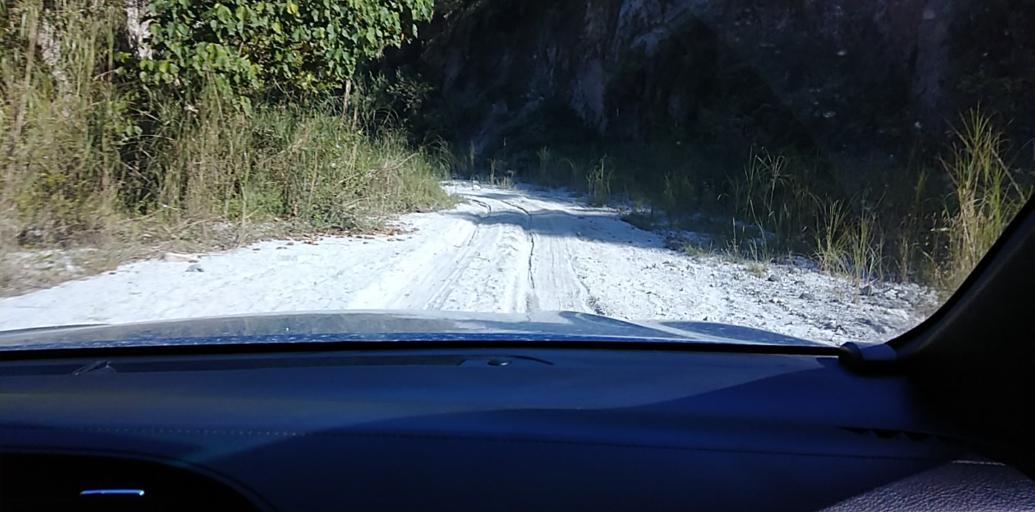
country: PH
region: Central Luzon
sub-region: Province of Pampanga
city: Dolores
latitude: 15.1646
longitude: 120.4720
